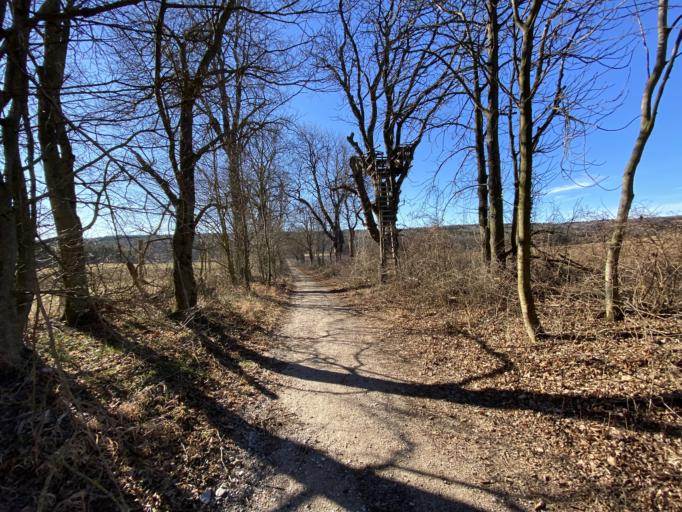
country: AT
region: Lower Austria
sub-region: Politischer Bezirk Baden
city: Berndorf
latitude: 47.9744
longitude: 16.1446
